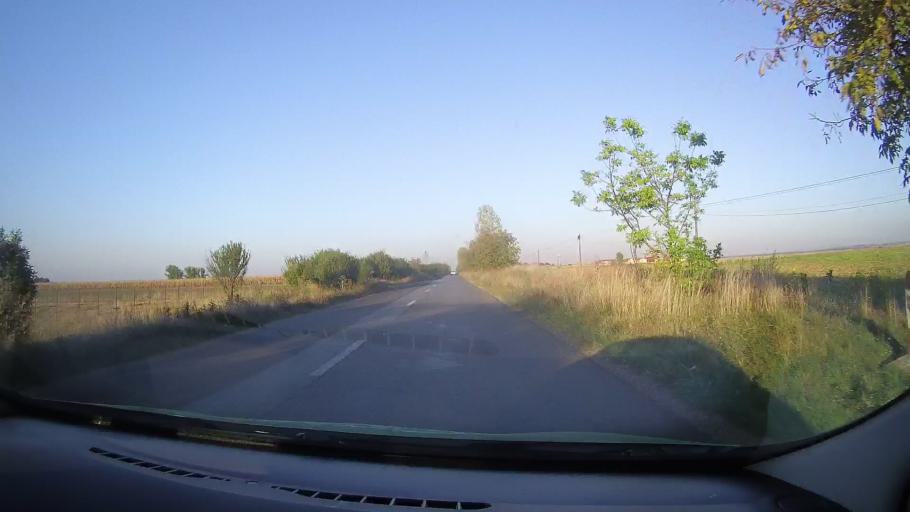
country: RO
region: Bihor
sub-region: Comuna Biharea
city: Biharea
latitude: 47.1696
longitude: 21.9552
